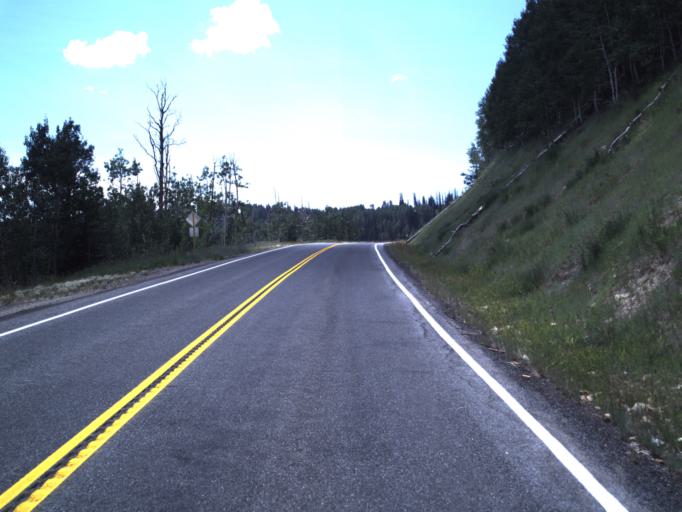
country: US
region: Utah
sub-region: Sanpete County
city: Fairview
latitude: 39.6826
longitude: -111.2136
